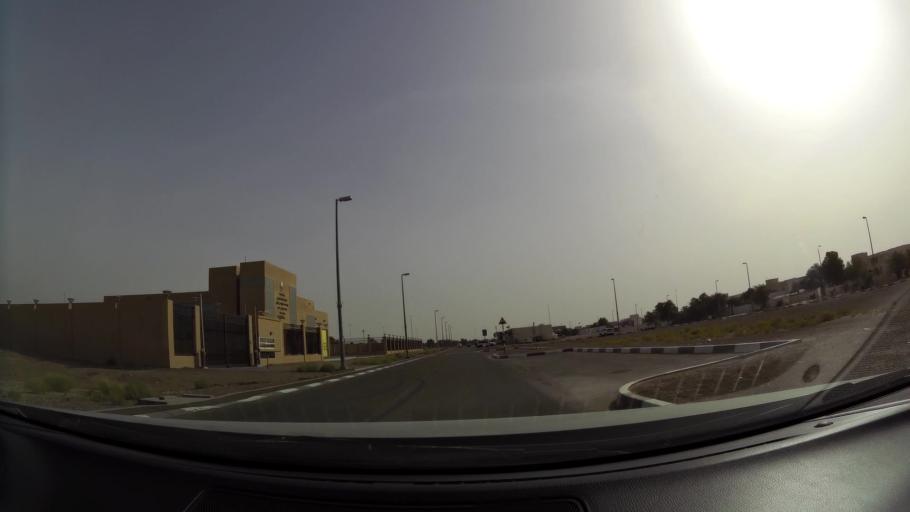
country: AE
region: Abu Dhabi
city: Al Ain
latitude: 24.2053
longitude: 55.5948
